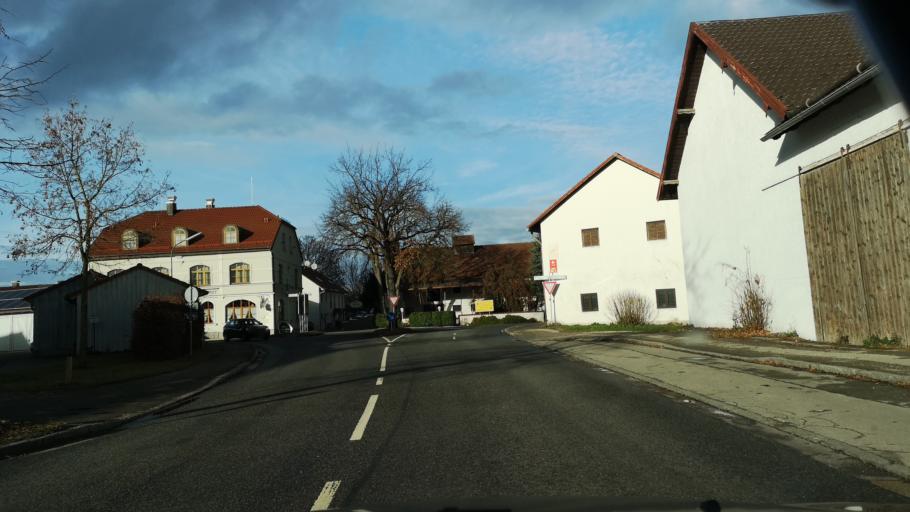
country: DE
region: Bavaria
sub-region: Upper Bavaria
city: Pliening
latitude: 48.1976
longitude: 11.7986
